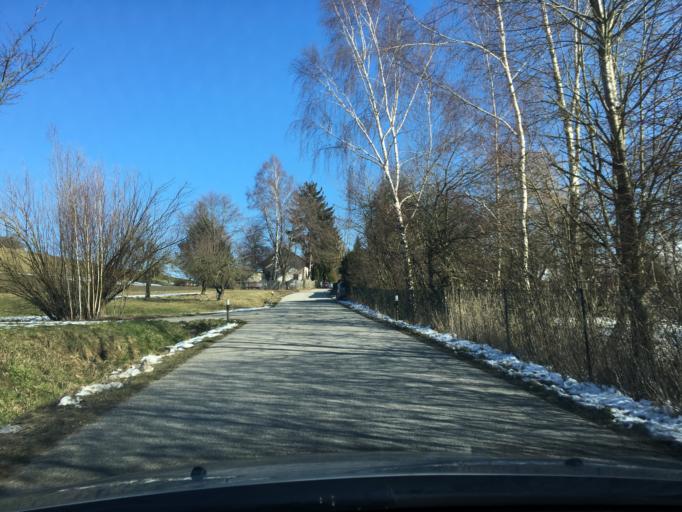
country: DE
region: Bavaria
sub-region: Lower Bavaria
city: Tiefenbach
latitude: 48.4762
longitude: 12.0909
